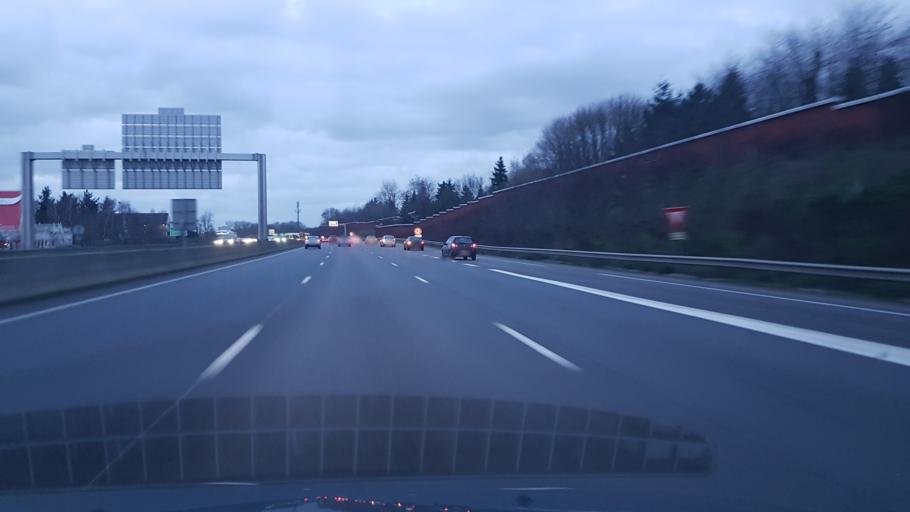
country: FR
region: Ile-de-France
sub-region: Departement de l'Essonne
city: Saint-Germain-les-Corbeil
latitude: 48.6315
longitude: 2.4934
